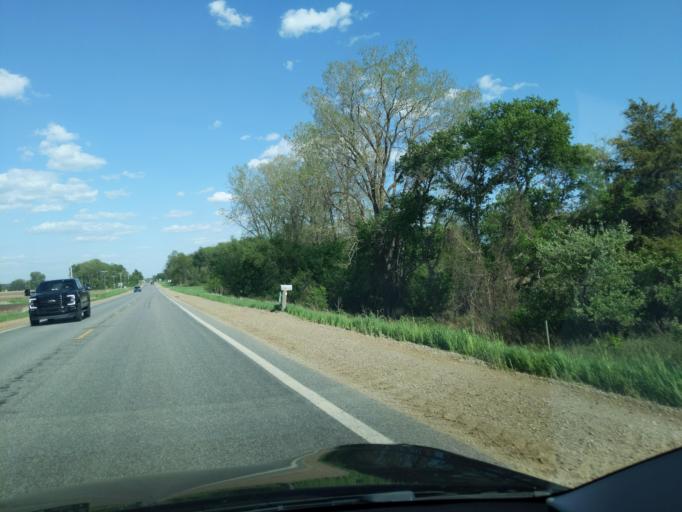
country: US
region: Michigan
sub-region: Ionia County
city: Lake Odessa
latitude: 42.7559
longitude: -85.0569
